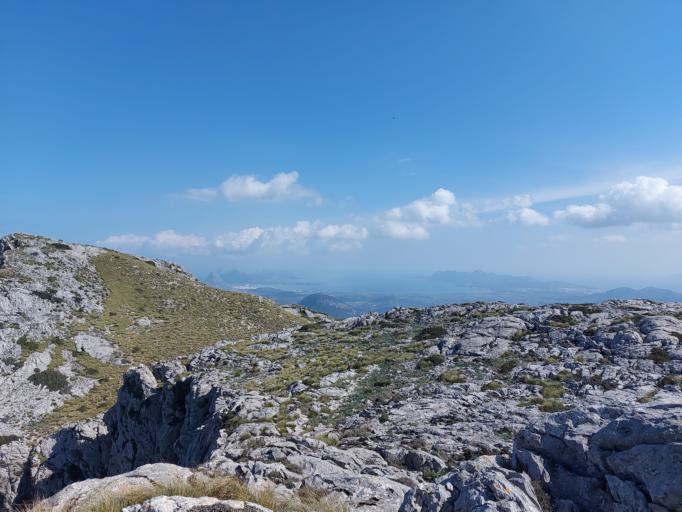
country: ES
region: Balearic Islands
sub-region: Illes Balears
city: Pollenca
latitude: 39.8490
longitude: 2.9657
